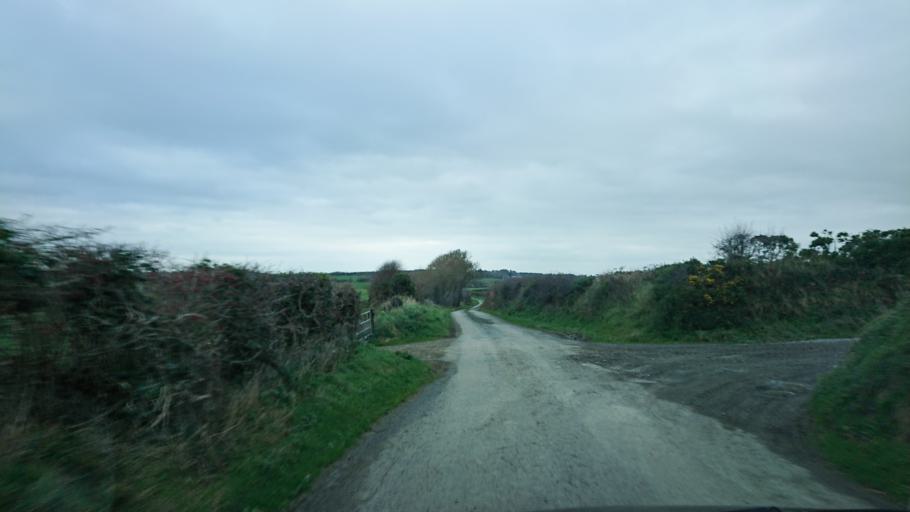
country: IE
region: Munster
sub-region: Waterford
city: Dunmore East
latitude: 52.1807
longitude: -7.0445
